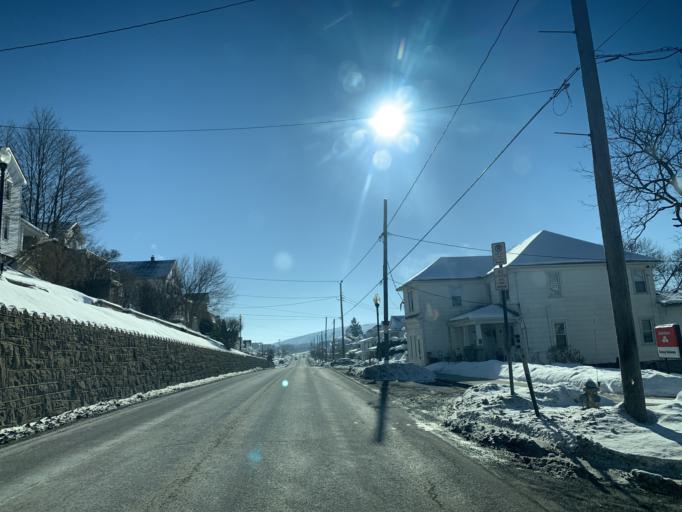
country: US
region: Maryland
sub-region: Allegany County
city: Frostburg
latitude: 39.6539
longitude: -78.9202
